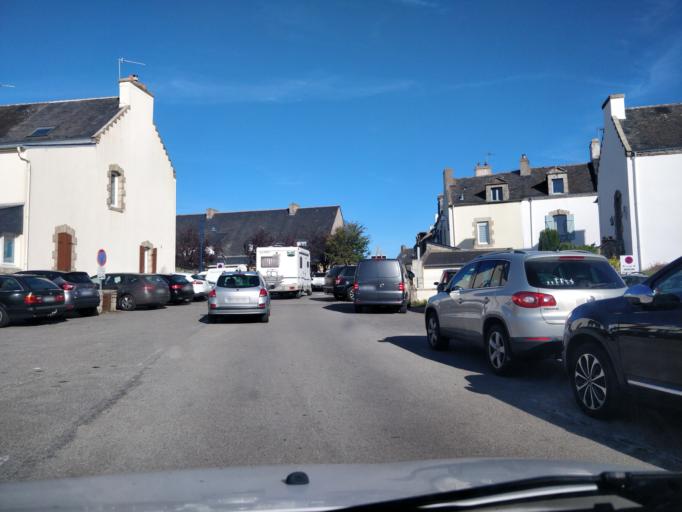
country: FR
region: Brittany
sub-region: Departement du Morbihan
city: Locmariaquer
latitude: 47.5696
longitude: -2.9444
